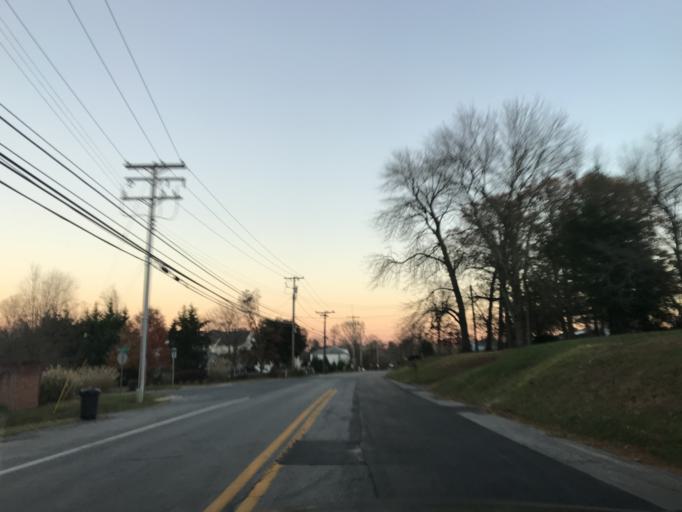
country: US
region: Maryland
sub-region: Howard County
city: West Elkridge
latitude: 39.2125
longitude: -76.7614
